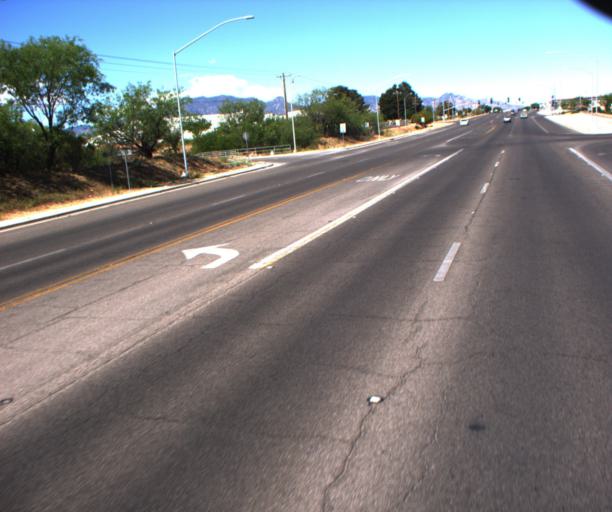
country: US
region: Arizona
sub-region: Cochise County
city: Sierra Vista
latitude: 31.5547
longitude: -110.2525
